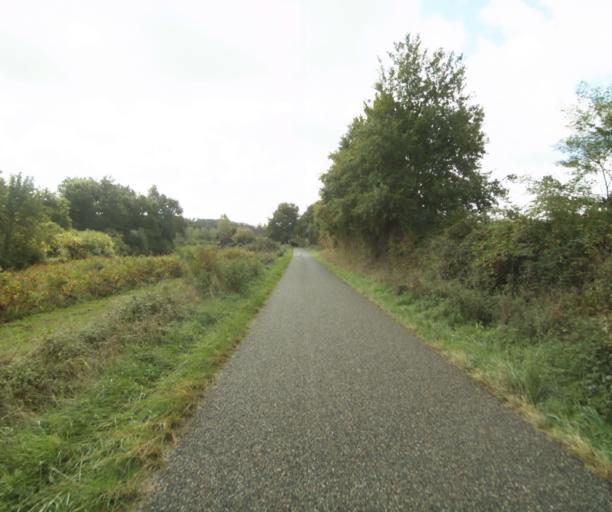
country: FR
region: Midi-Pyrenees
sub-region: Departement du Gers
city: Nogaro
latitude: 43.8302
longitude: -0.0971
